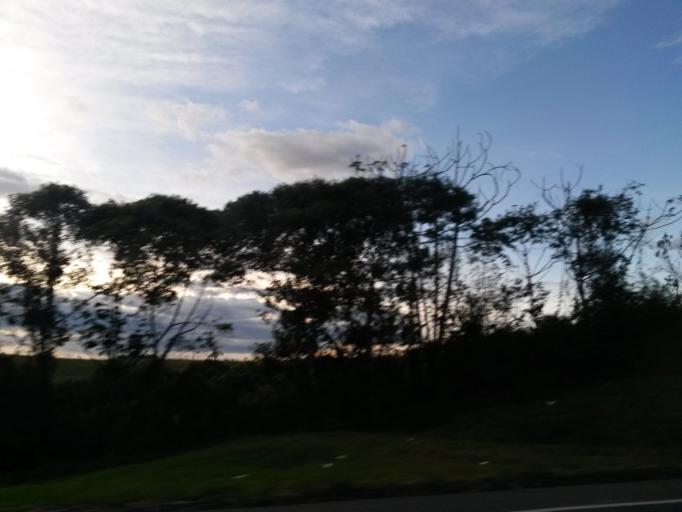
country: CO
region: Cauca
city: Popayan
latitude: 2.4697
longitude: -76.6239
